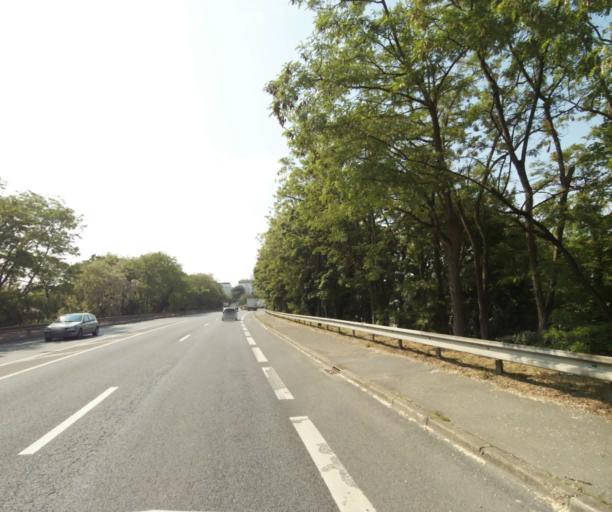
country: FR
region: Ile-de-France
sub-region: Departement du Val-d'Oise
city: Argenteuil
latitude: 48.9501
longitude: 2.2370
